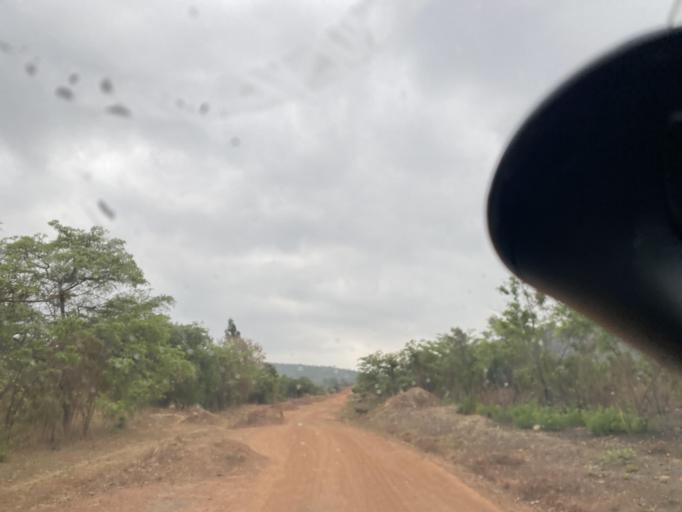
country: ZM
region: Lusaka
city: Chongwe
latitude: -15.1890
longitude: 28.7636
